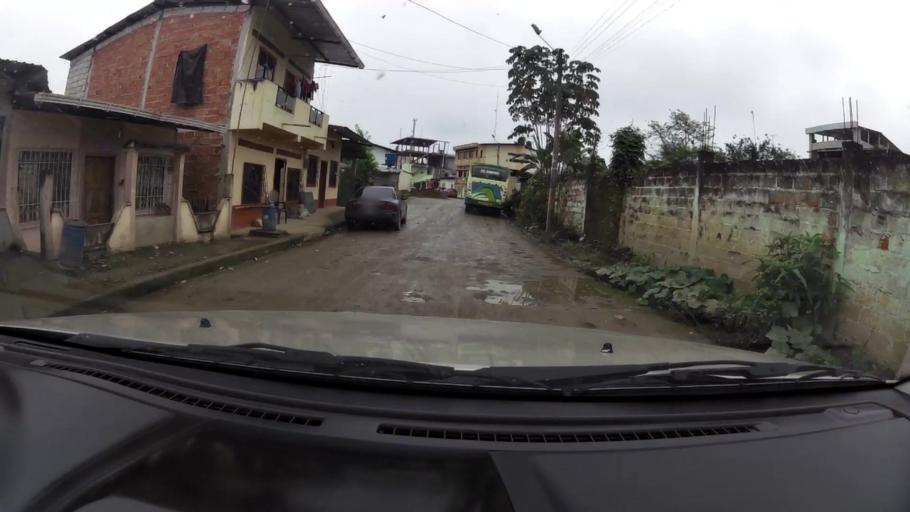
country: EC
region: Guayas
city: Balao
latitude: -3.0637
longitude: -79.7463
